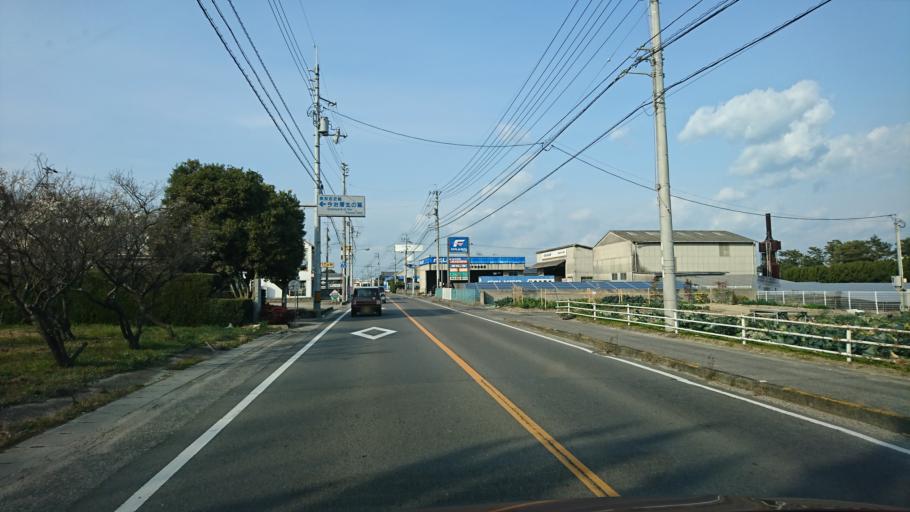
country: JP
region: Ehime
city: Saijo
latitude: 34.0310
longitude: 133.0361
